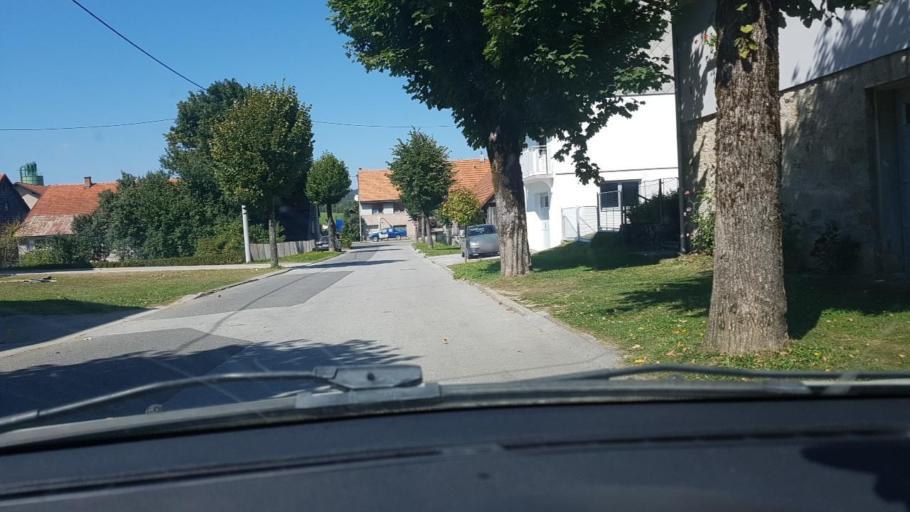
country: SI
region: Kostel
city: Kostel
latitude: 45.3729
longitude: 14.9387
